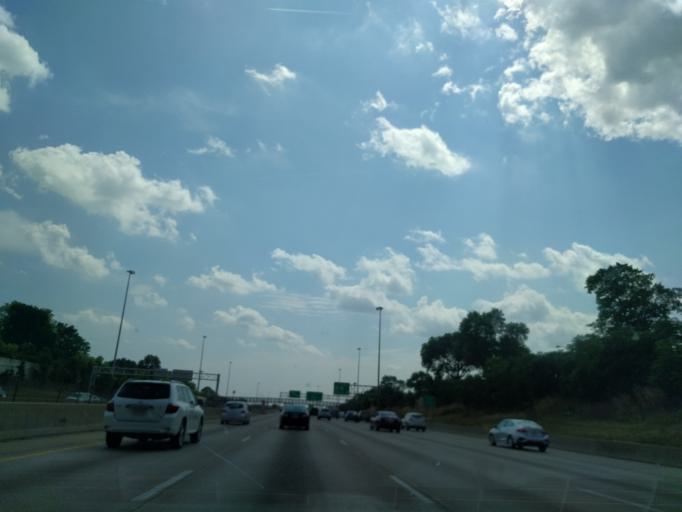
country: US
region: Illinois
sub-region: Cook County
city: Calumet Park
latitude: 41.7291
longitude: -87.6247
